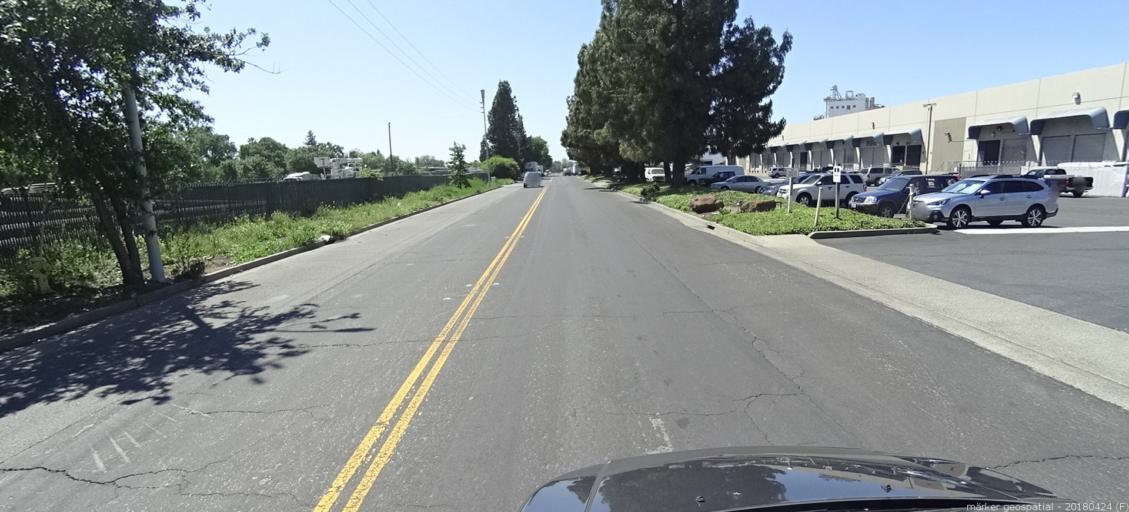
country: US
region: California
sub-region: Yolo County
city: West Sacramento
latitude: 38.5694
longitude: -121.5386
